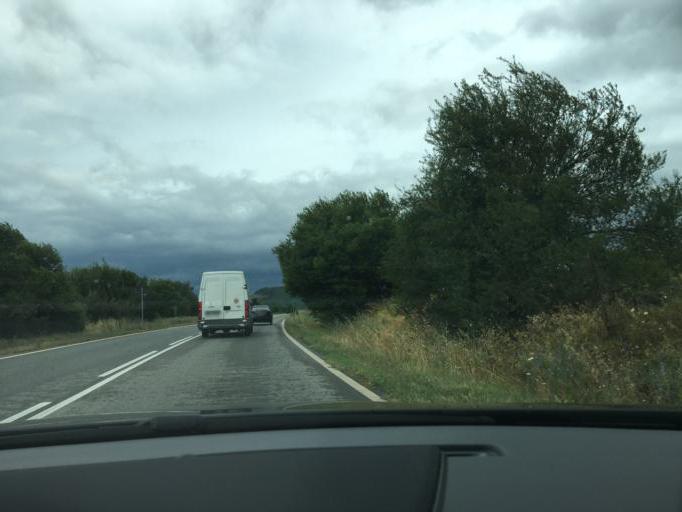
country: BG
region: Kyustendil
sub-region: Obshtina Bobovdol
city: Bobovdol
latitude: 42.2737
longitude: 22.9919
